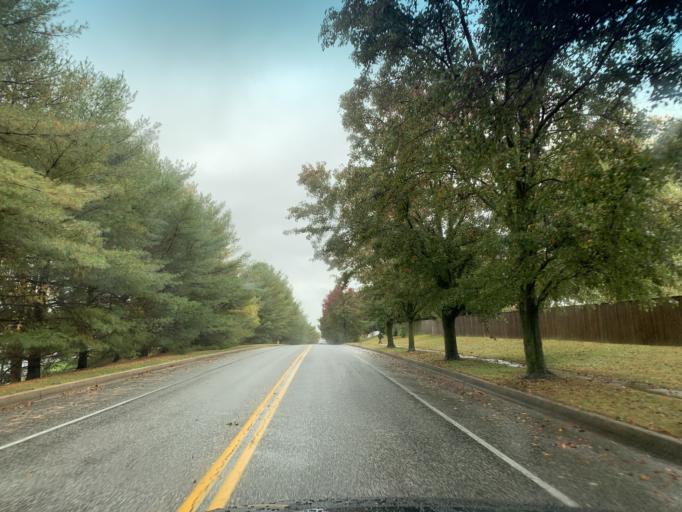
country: US
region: Maryland
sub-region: Harford County
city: South Bel Air
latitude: 39.5355
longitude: -76.3235
